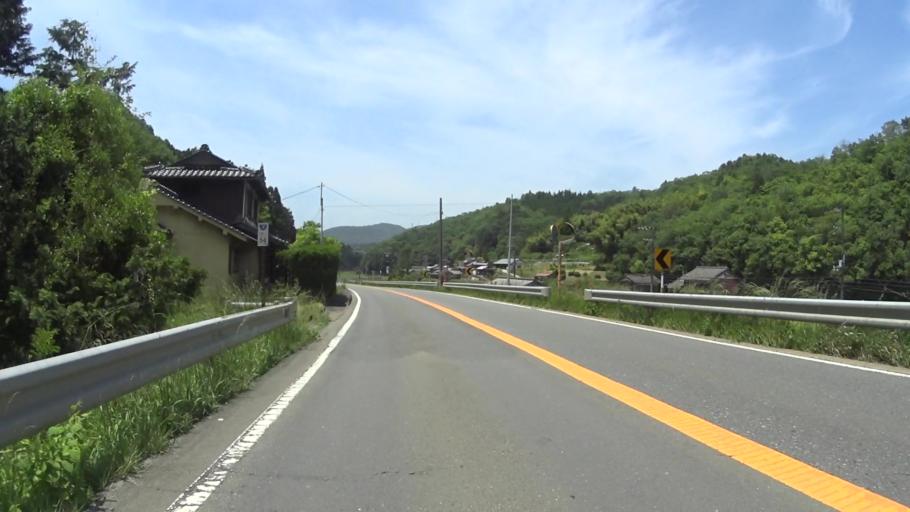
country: JP
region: Kyoto
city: Ayabe
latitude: 35.1831
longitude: 135.3440
